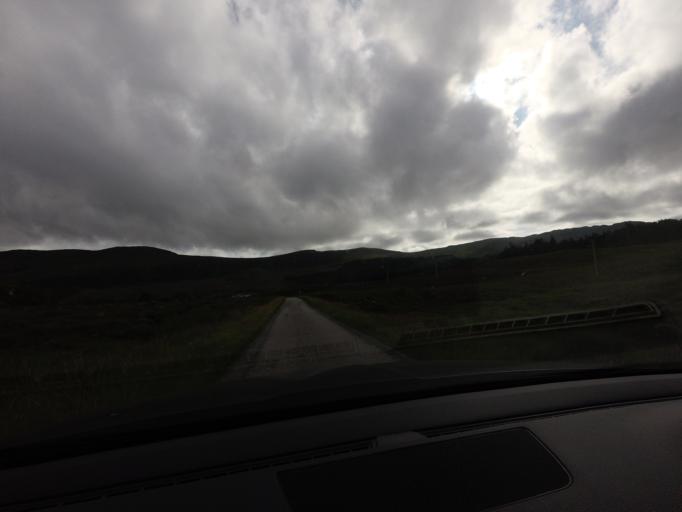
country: GB
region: Scotland
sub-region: Highland
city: Ullapool
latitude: 58.3160
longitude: -4.9116
